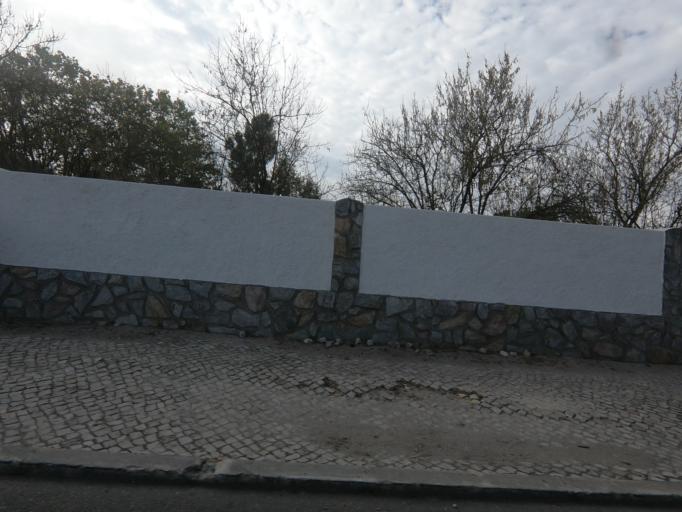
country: PT
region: Setubal
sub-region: Seixal
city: Amora
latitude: 38.5989
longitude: -9.1403
